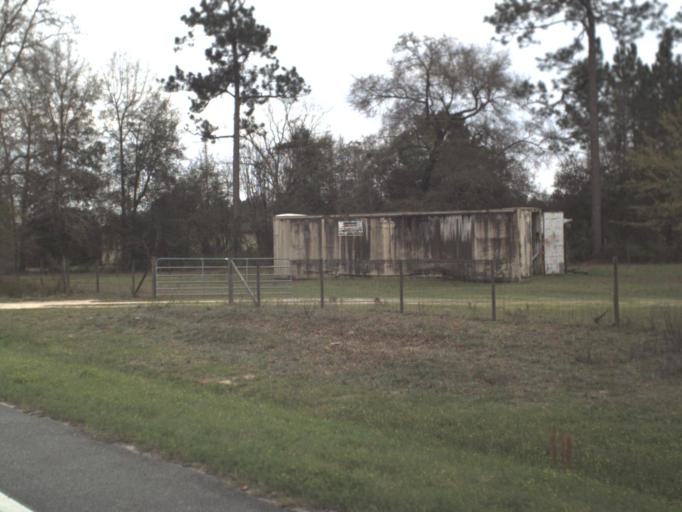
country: US
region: Florida
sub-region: Gulf County
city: Wewahitchka
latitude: 30.2623
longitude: -85.2393
